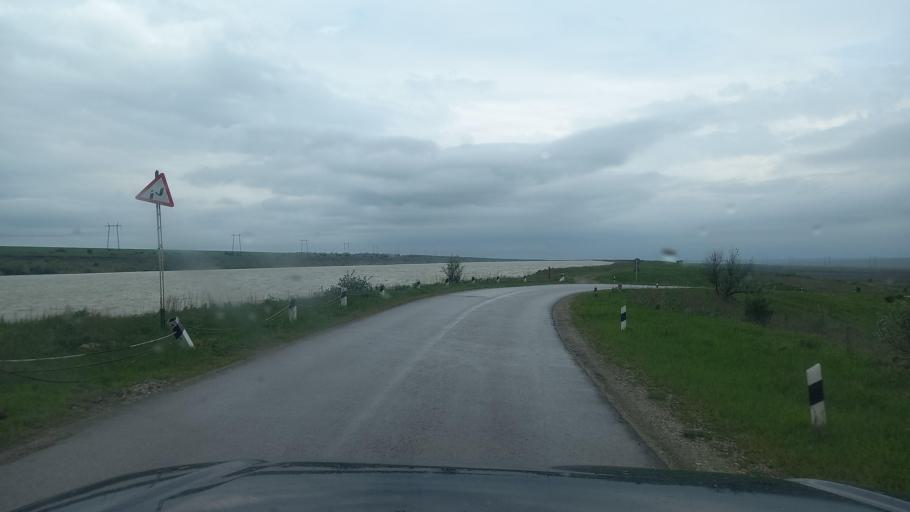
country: RU
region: Stavropol'skiy
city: Nevinnomyssk
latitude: 44.5929
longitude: 42.2295
